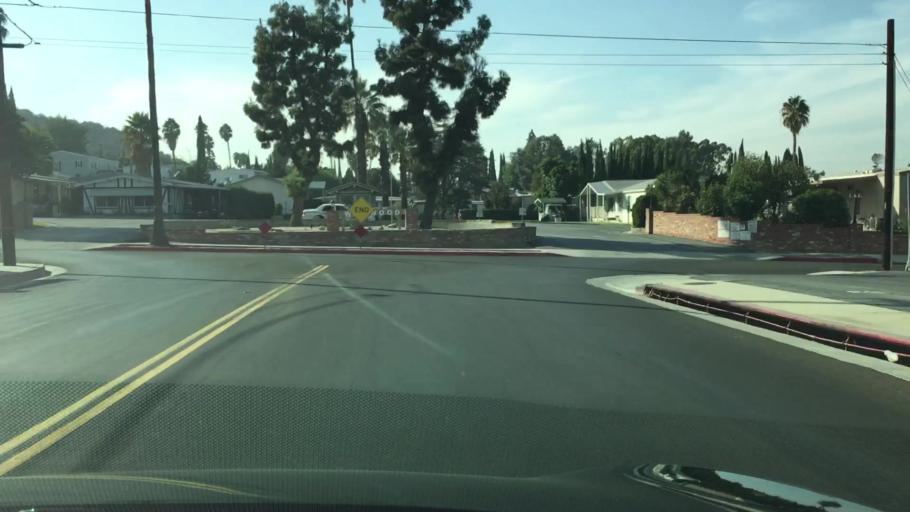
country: US
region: California
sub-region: Los Angeles County
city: Avocado Heights
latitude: 34.0249
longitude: -117.9897
